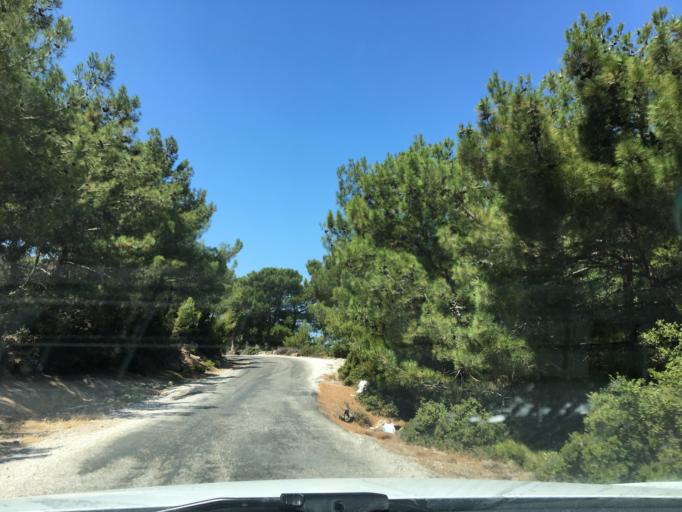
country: TR
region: Canakkale
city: Gulpinar
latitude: 39.4983
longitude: 26.1293
